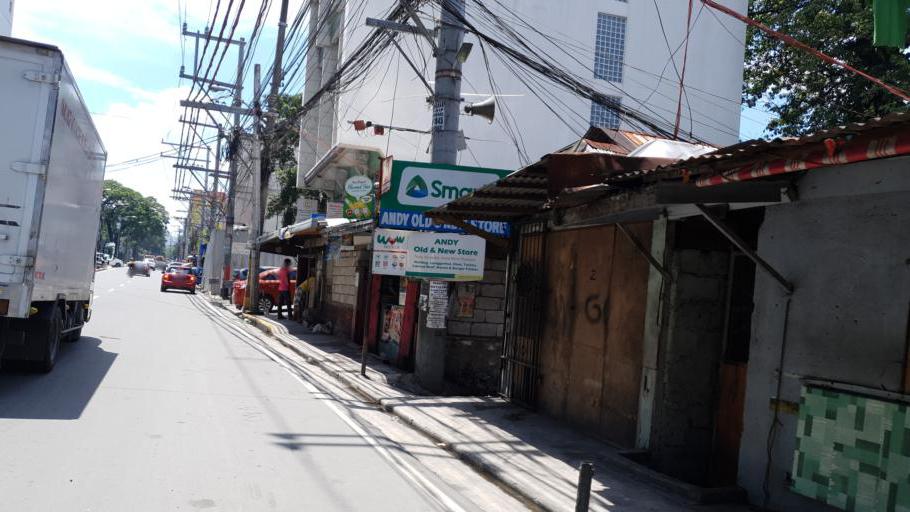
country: PH
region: Metro Manila
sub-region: San Juan
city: San Juan
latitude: 14.6000
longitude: 121.0138
